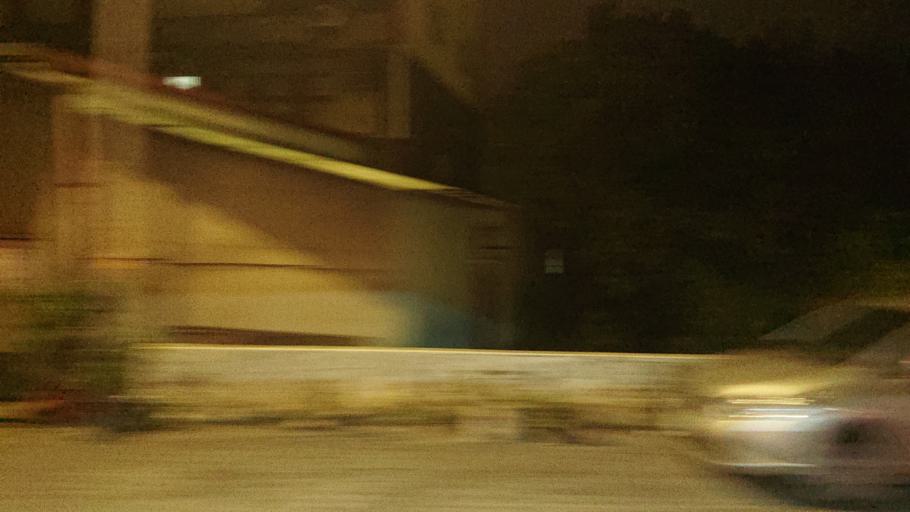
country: TW
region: Taipei
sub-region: Taipei
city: Banqiao
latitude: 24.9452
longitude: 121.4039
